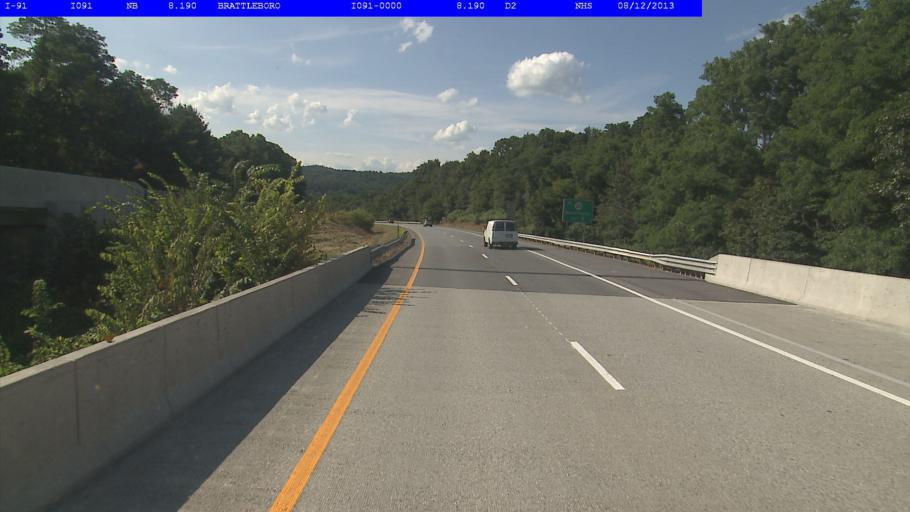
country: US
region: Vermont
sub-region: Windham County
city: Brattleboro
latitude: 42.8446
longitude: -72.5731
